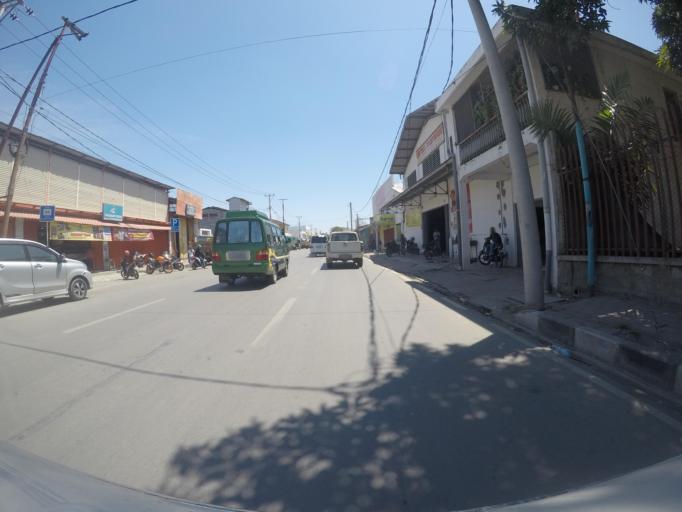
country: TL
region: Dili
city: Dili
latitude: -8.5554
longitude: 125.5857
